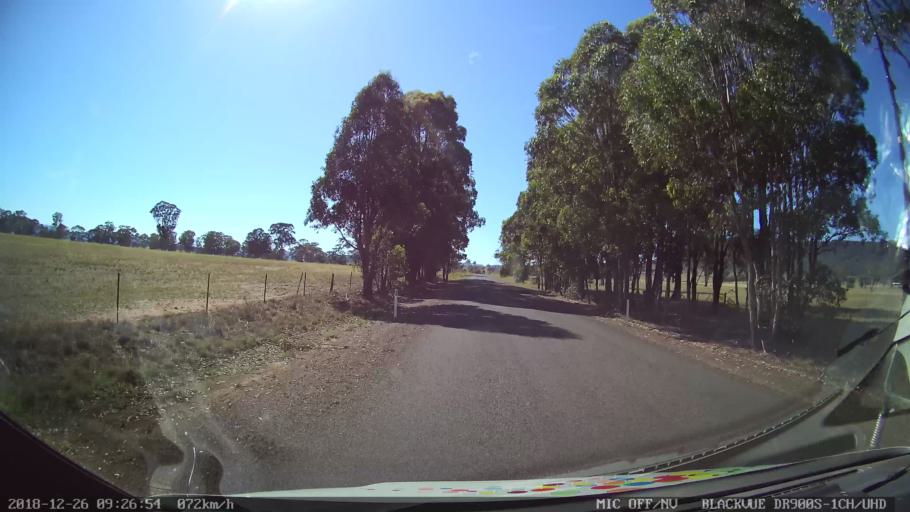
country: AU
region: New South Wales
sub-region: Mid-Western Regional
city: Kandos
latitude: -32.8315
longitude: 150.0123
